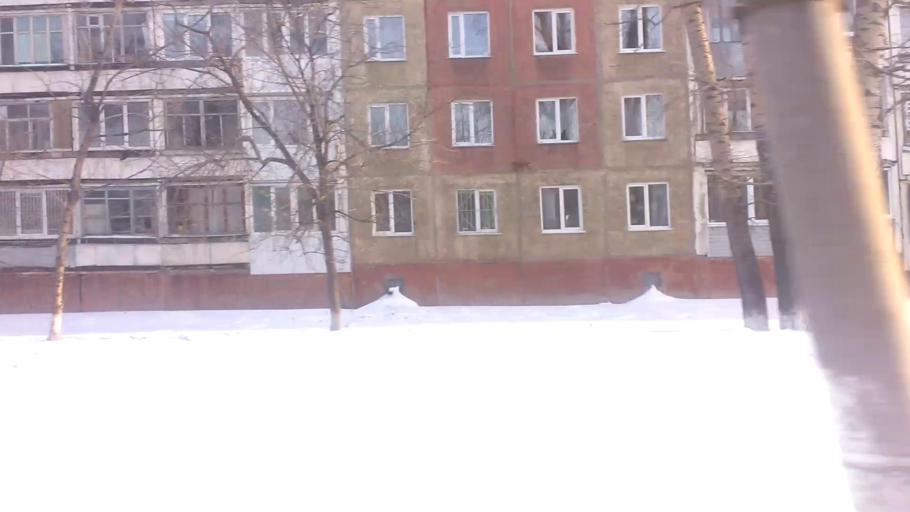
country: RU
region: Altai Krai
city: Novosilikatnyy
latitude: 53.3726
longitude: 83.6632
